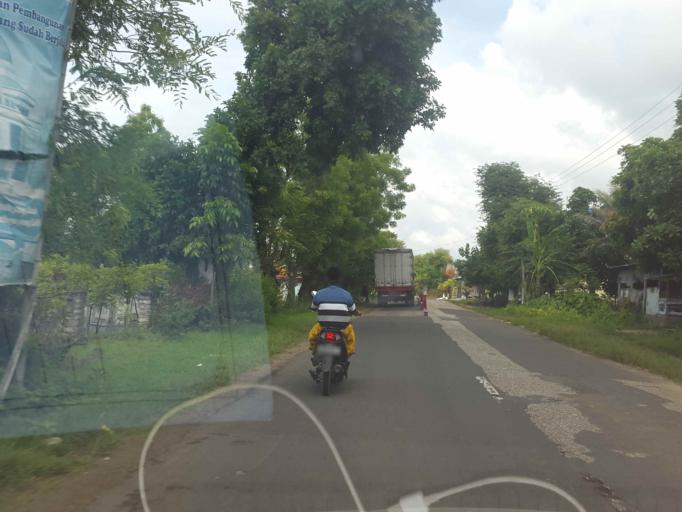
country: ID
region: East Java
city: Pesisir
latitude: -7.1188
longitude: 113.7712
